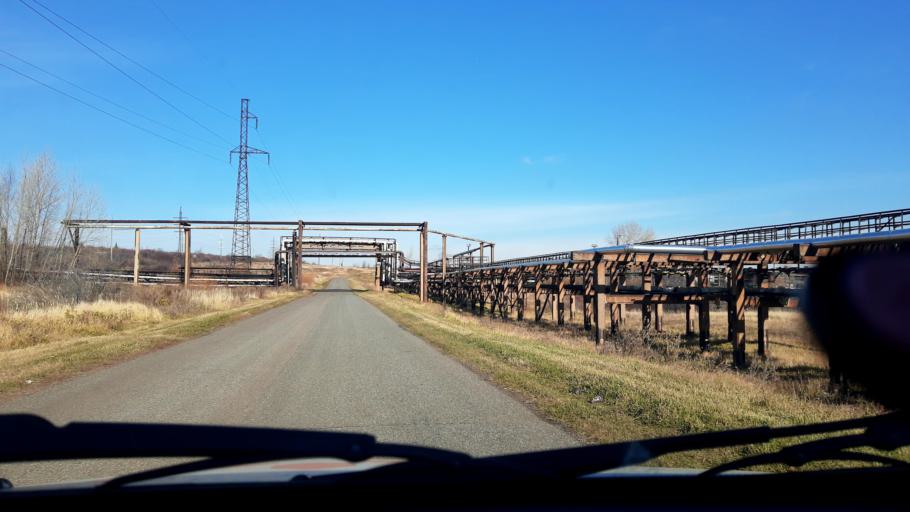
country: RU
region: Bashkortostan
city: Blagoveshchensk
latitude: 54.8866
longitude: 56.1022
